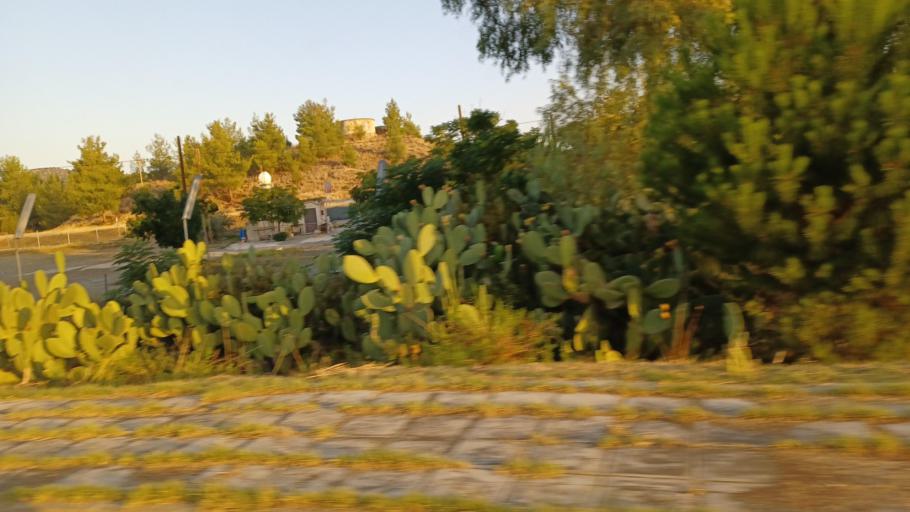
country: CY
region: Lefkosia
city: Lythrodontas
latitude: 34.9478
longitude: 33.2917
